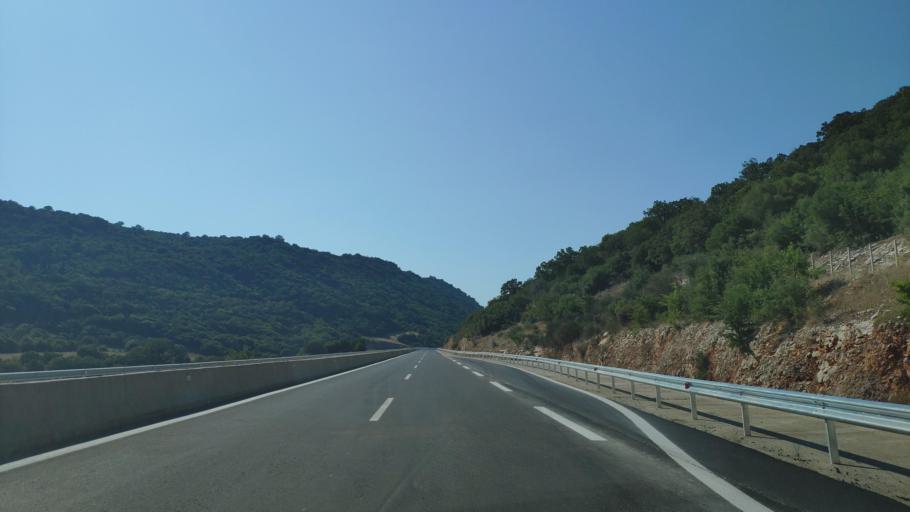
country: GR
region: West Greece
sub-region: Nomos Aitolias kai Akarnanias
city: Katouna
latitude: 38.8491
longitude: 21.0956
